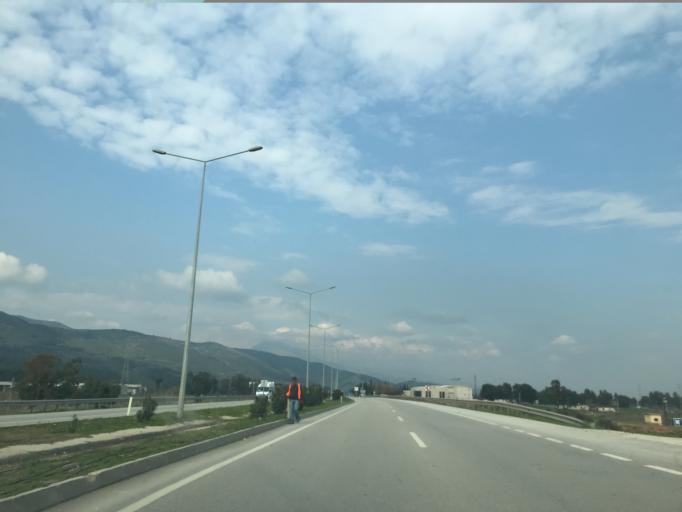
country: TR
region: Hatay
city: Serinyol
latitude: 36.3633
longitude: 36.2226
